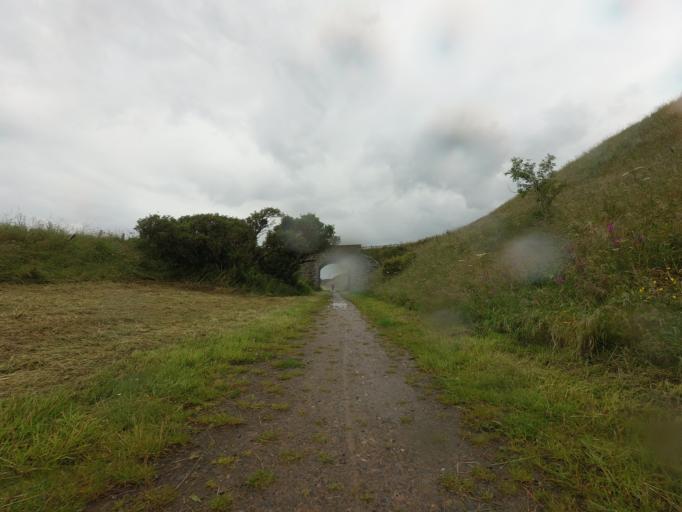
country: GB
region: Scotland
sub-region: Moray
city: Buckie
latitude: 57.6656
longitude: -3.0052
